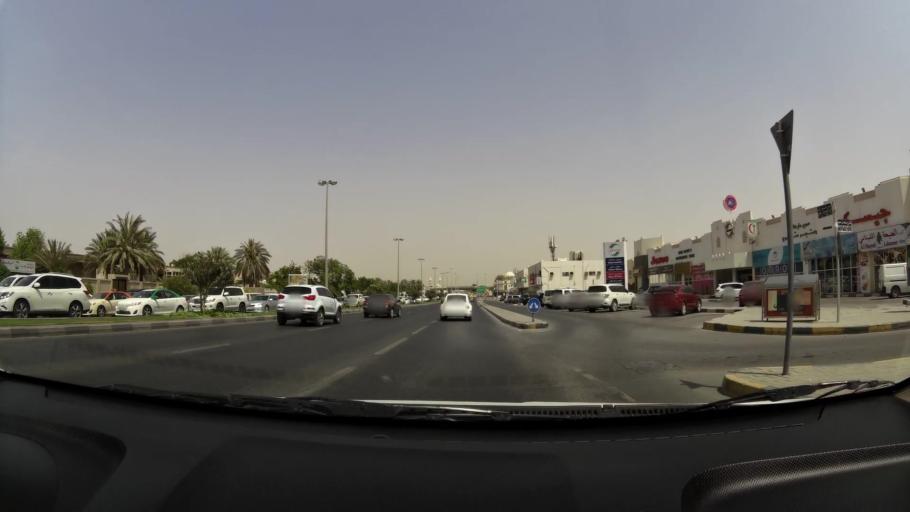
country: AE
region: Ash Shariqah
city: Sharjah
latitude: 25.3554
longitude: 55.4063
